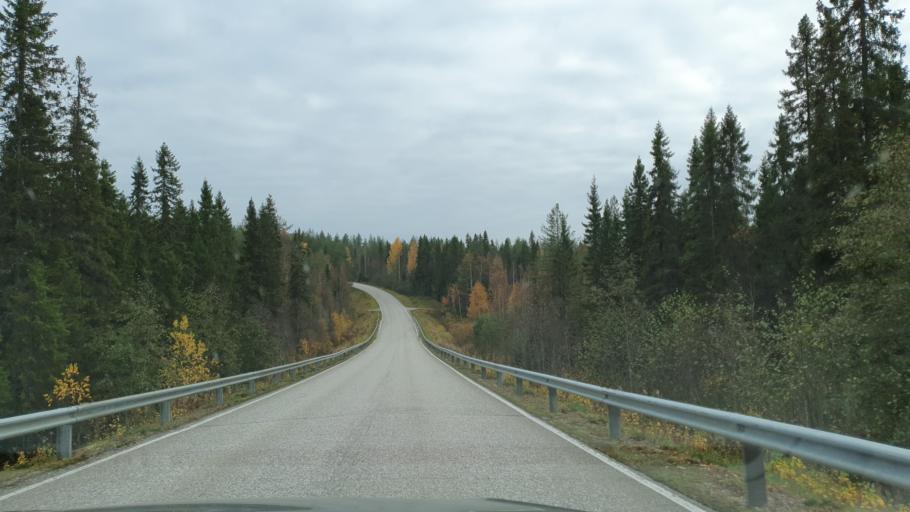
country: FI
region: Kainuu
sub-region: Kajaani
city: Ristijaervi
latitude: 64.4734
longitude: 28.2886
